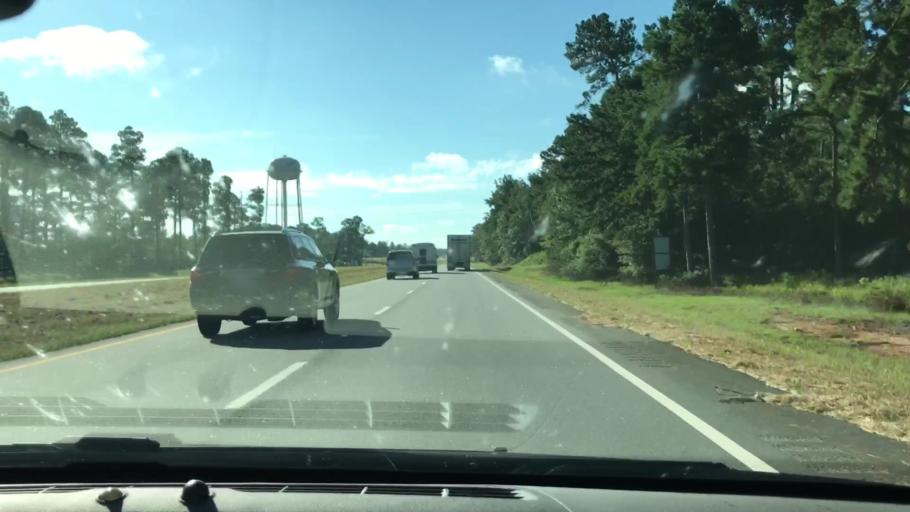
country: US
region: Georgia
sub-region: Dougherty County
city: Albany
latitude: 31.6423
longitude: -84.2544
